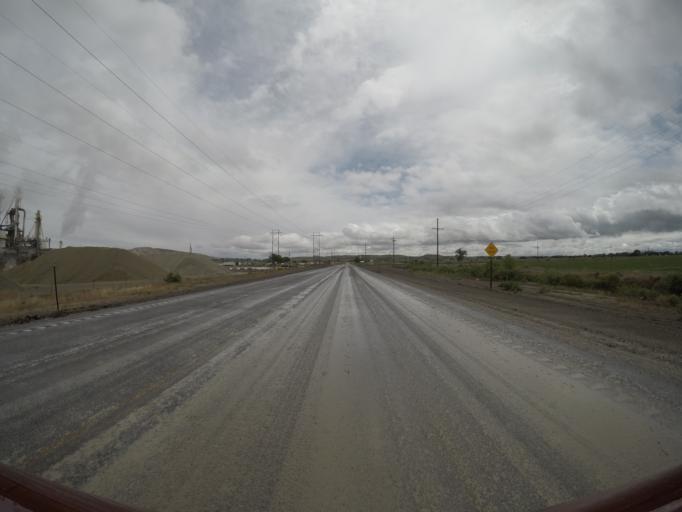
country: US
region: Wyoming
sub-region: Big Horn County
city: Lovell
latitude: 44.8552
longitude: -108.3316
